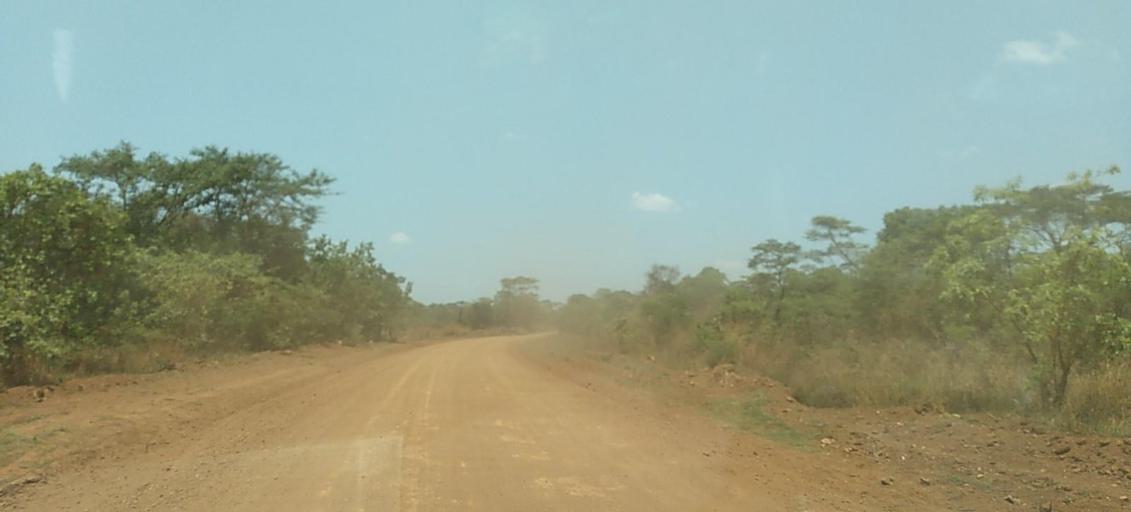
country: ZM
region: Copperbelt
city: Mpongwe
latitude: -13.5183
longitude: 27.9738
